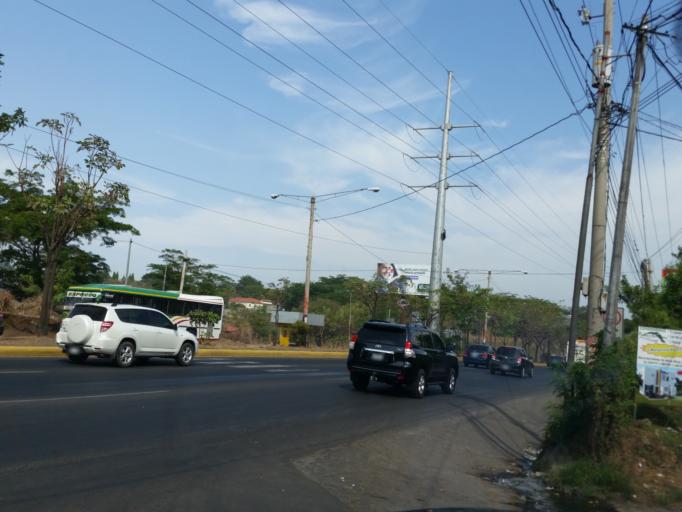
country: NI
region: Managua
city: Managua
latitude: 12.0940
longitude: -86.2380
